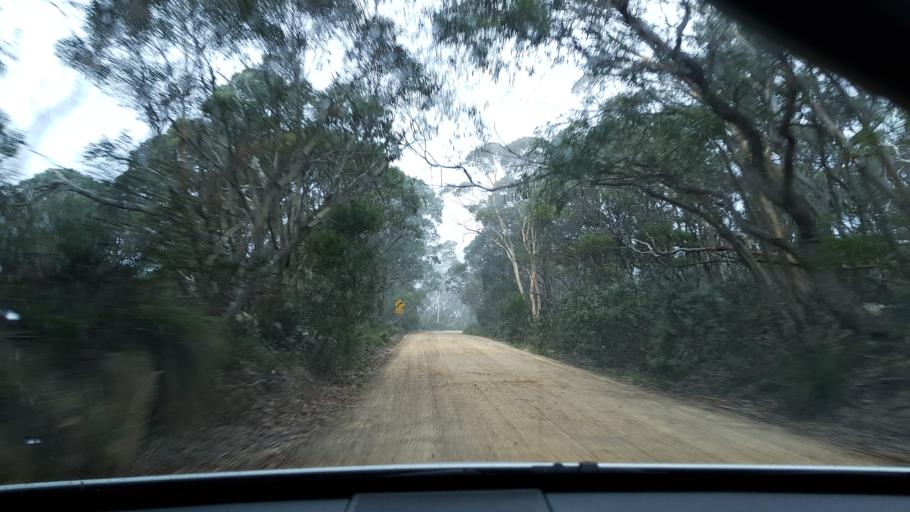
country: AU
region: New South Wales
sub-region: Oberon
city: Oberon
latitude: -33.9887
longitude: 150.0672
